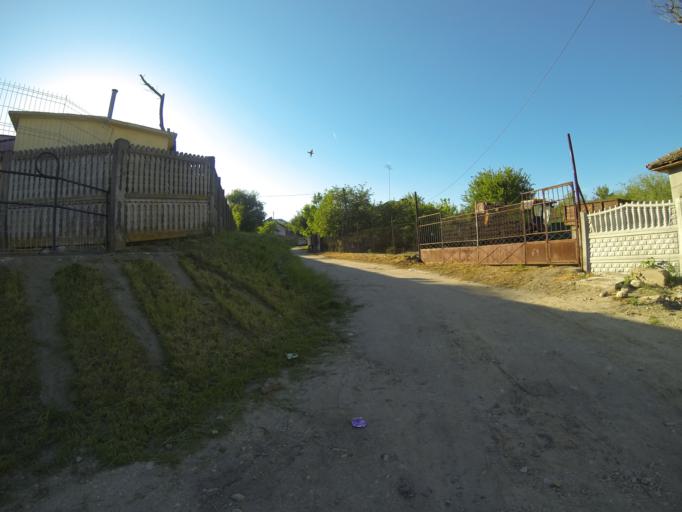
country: RO
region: Dolj
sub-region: Comuna Segarcea
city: Segarcea
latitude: 44.0965
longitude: 23.7410
